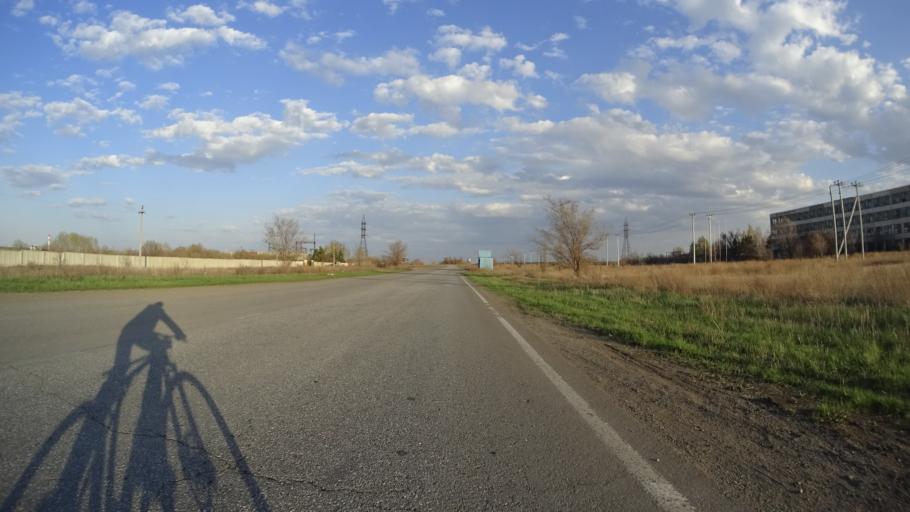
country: RU
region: Chelyabinsk
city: Troitsk
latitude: 54.0643
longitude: 61.5693
